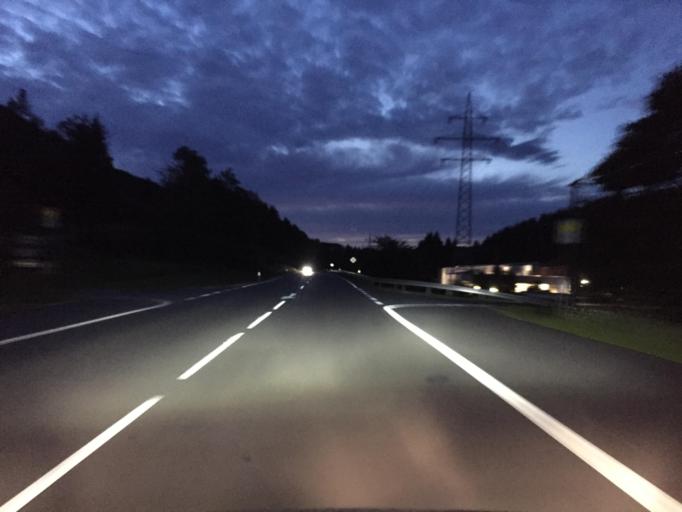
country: DE
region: Baden-Wuerttemberg
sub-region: Freiburg Region
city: Blumberg
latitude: 47.8489
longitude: 8.5538
